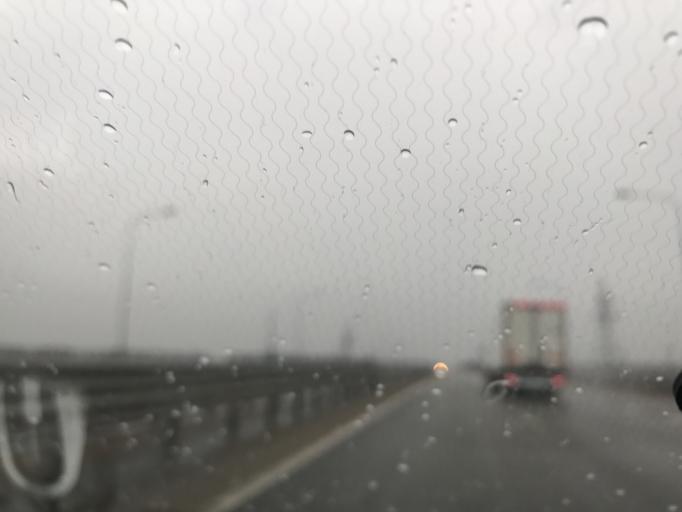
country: RU
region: Krasnodarskiy
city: Kislyakovskaya
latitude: 46.3301
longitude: 39.7897
